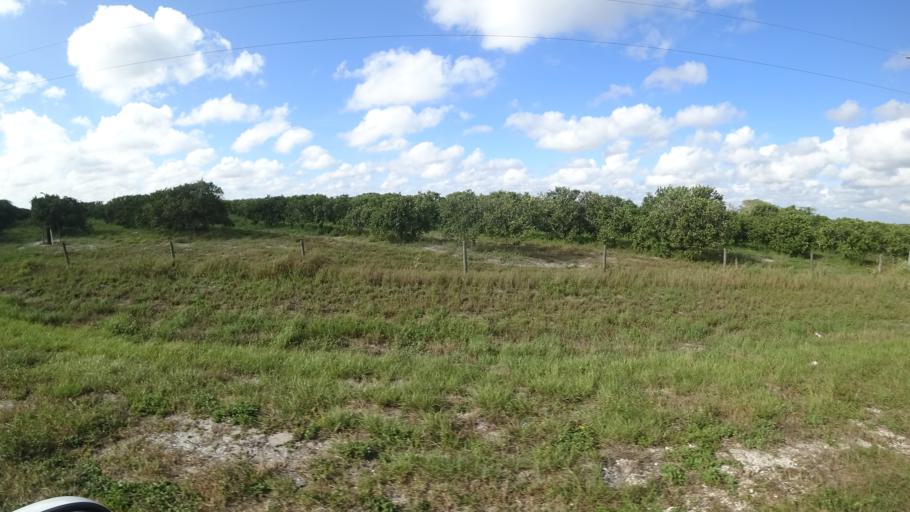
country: US
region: Florida
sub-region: Sarasota County
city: The Meadows
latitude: 27.4886
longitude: -82.3029
